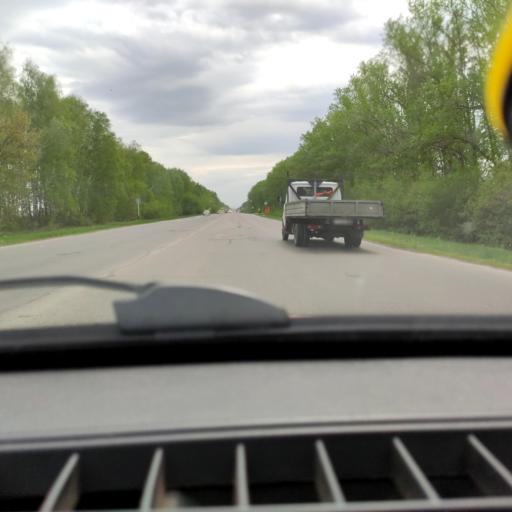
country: RU
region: Samara
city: Tol'yatti
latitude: 53.6277
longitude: 49.4165
